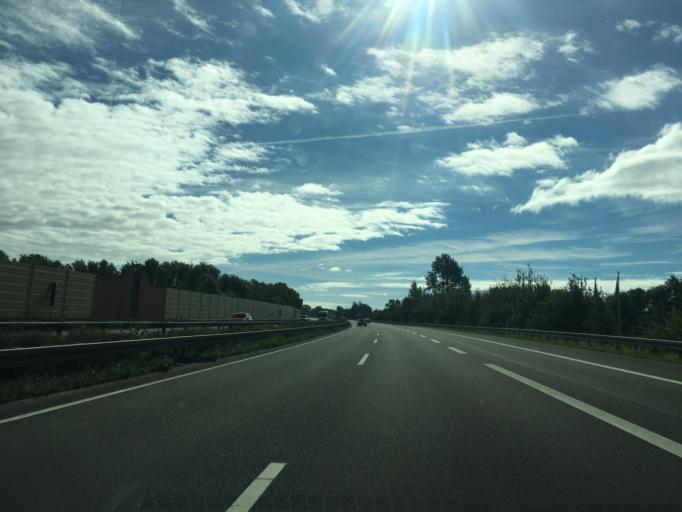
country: DE
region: Lower Saxony
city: Melle
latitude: 52.1955
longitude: 8.3183
